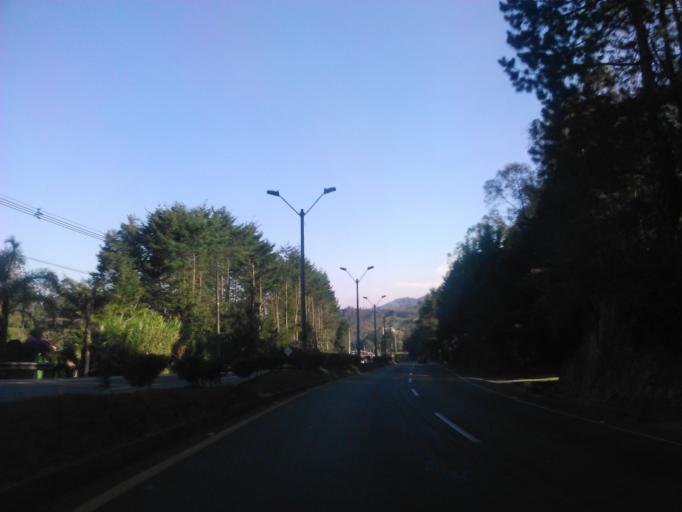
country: CO
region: Antioquia
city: Guarne
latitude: 6.3121
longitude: -75.4609
